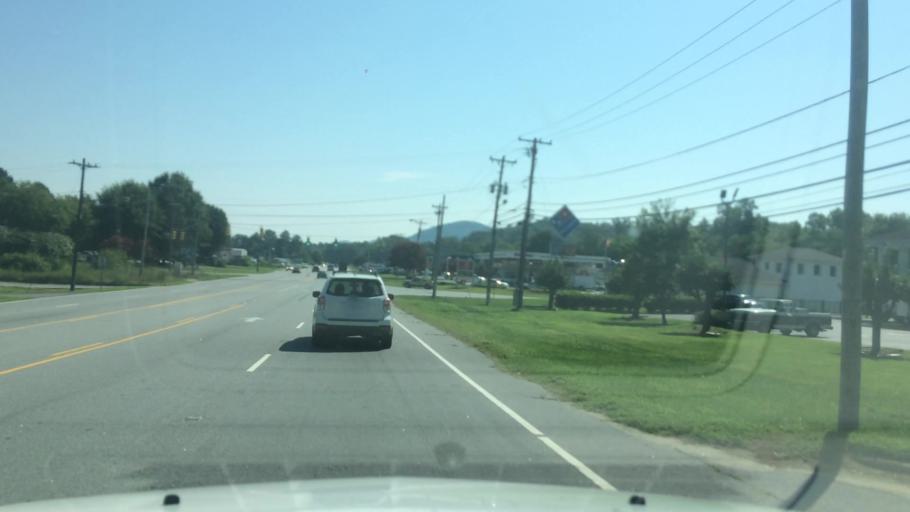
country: US
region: North Carolina
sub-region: Caldwell County
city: Lenoir
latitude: 35.9159
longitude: -81.5178
